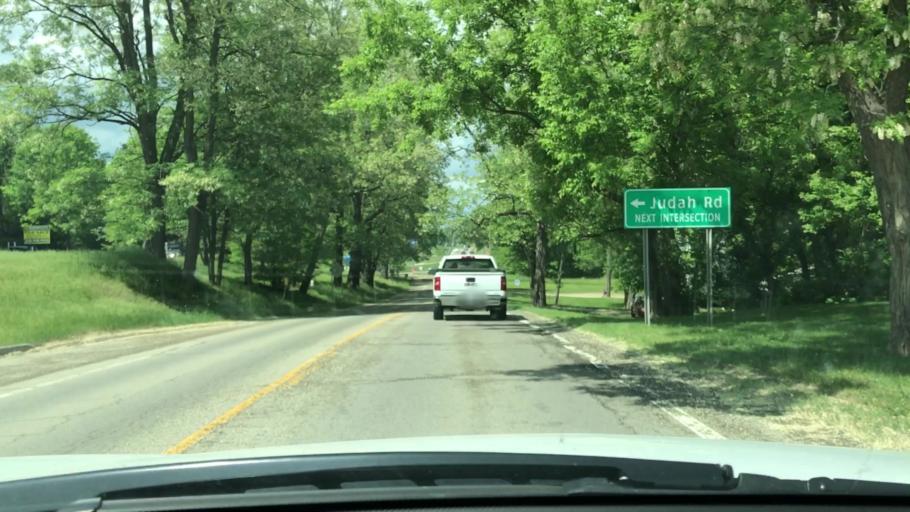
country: US
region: Michigan
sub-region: Oakland County
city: Auburn Hills
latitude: 42.7129
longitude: -83.2855
